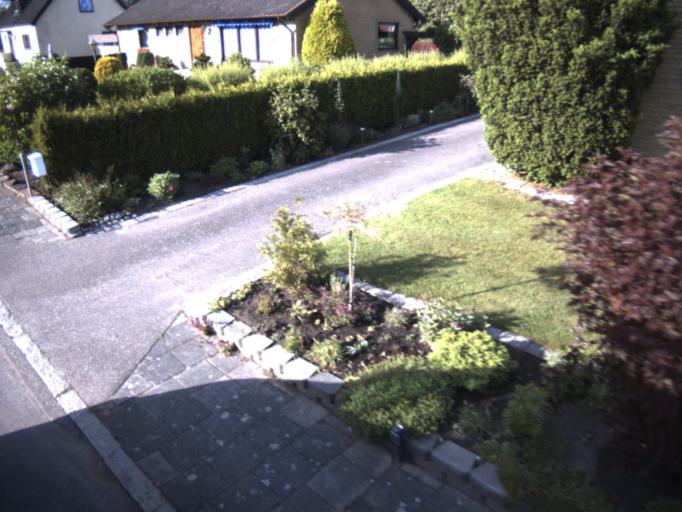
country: SE
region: Skane
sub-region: Helsingborg
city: Helsingborg
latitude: 56.0482
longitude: 12.7247
